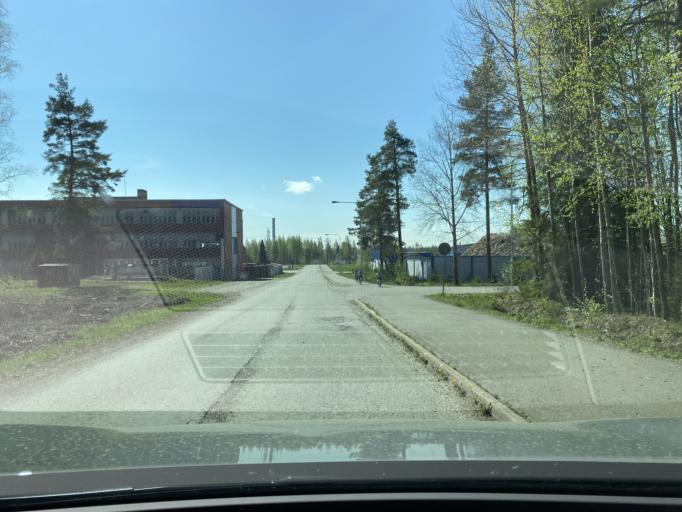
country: FI
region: Pirkanmaa
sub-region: Lounais-Pirkanmaa
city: Vammala
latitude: 61.3538
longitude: 22.8808
